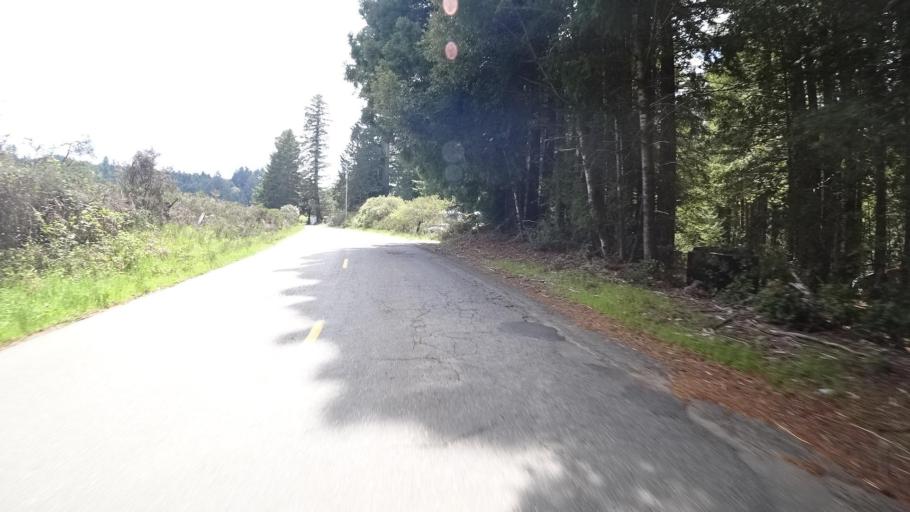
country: US
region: California
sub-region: Humboldt County
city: Redway
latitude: 40.0393
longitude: -123.9582
